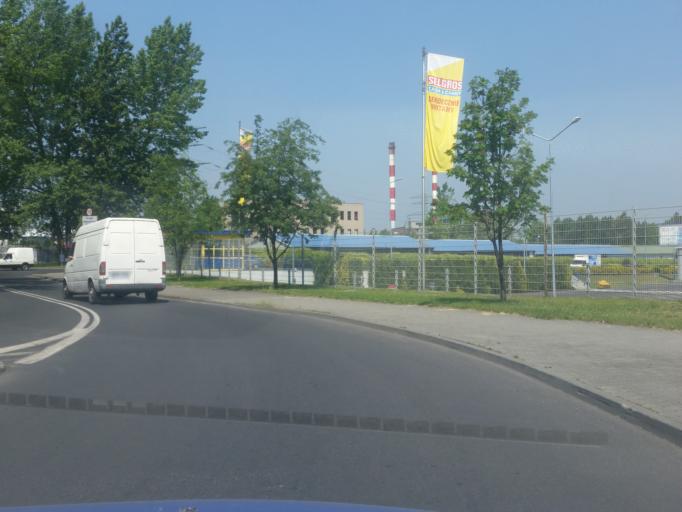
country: PL
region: Silesian Voivodeship
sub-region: Sosnowiec
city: Sosnowiec
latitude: 50.2556
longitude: 19.0897
